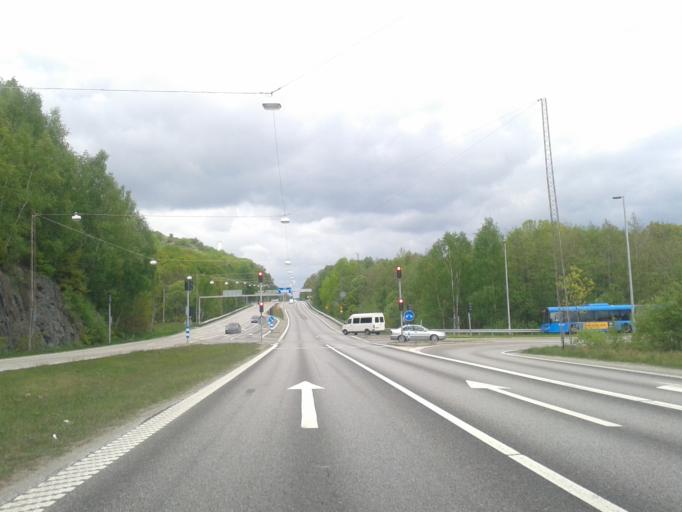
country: SE
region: Vaestra Goetaland
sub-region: Goteborg
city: Hammarkullen
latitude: 57.7941
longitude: 12.0425
